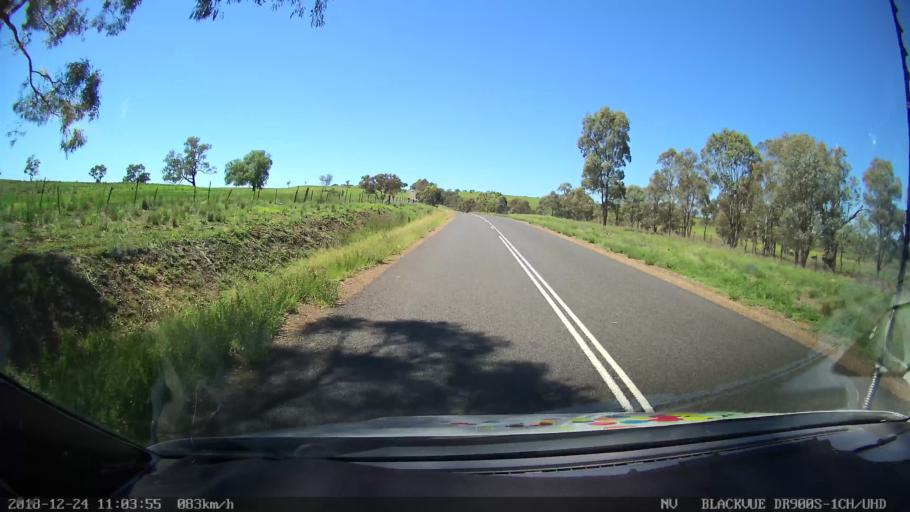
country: AU
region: New South Wales
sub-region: Upper Hunter Shire
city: Merriwa
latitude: -32.1028
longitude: 150.3691
